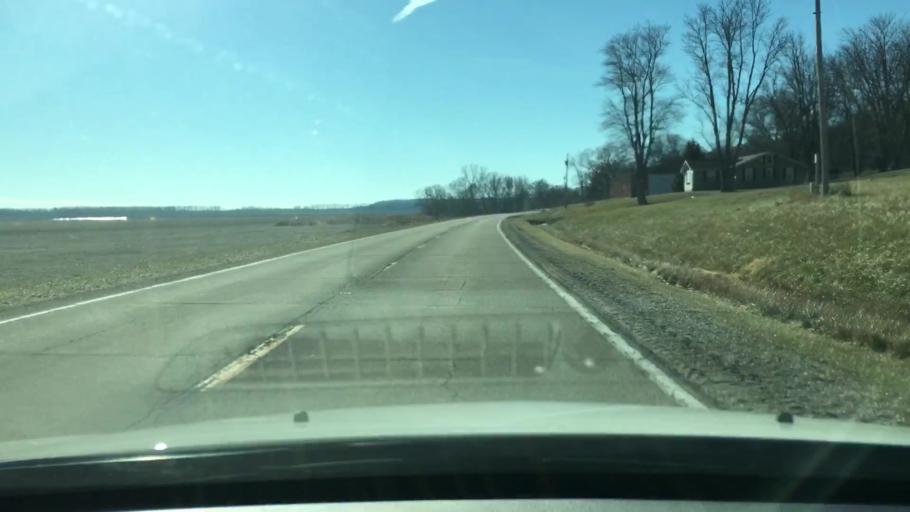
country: US
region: Illinois
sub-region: Mason County
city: Havana
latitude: 40.2560
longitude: -90.1798
